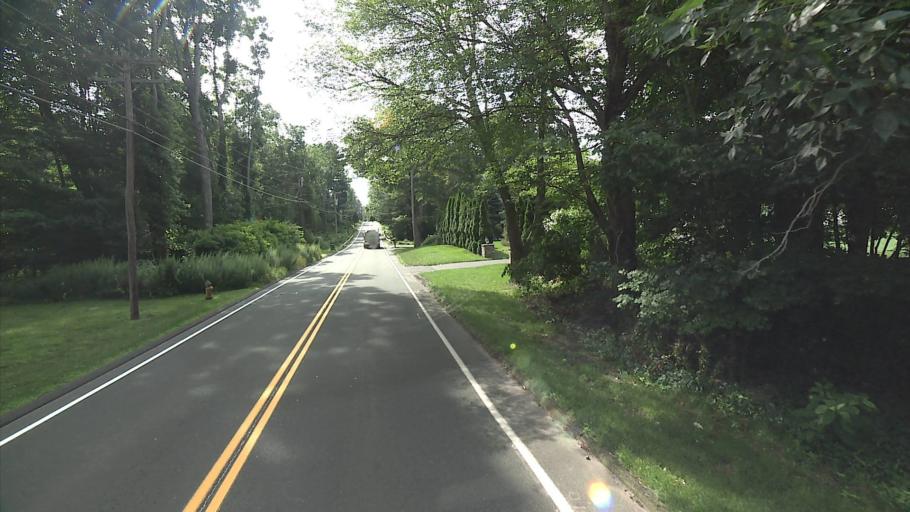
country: US
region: Connecticut
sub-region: New Haven County
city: Woodbridge
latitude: 41.3367
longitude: -73.0038
